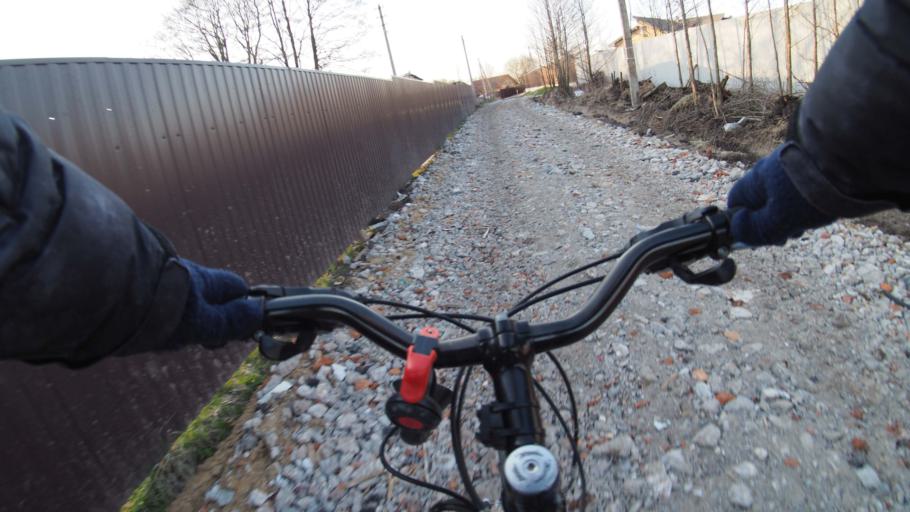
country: RU
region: Moskovskaya
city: Ramenskoye
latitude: 55.5637
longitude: 38.2924
